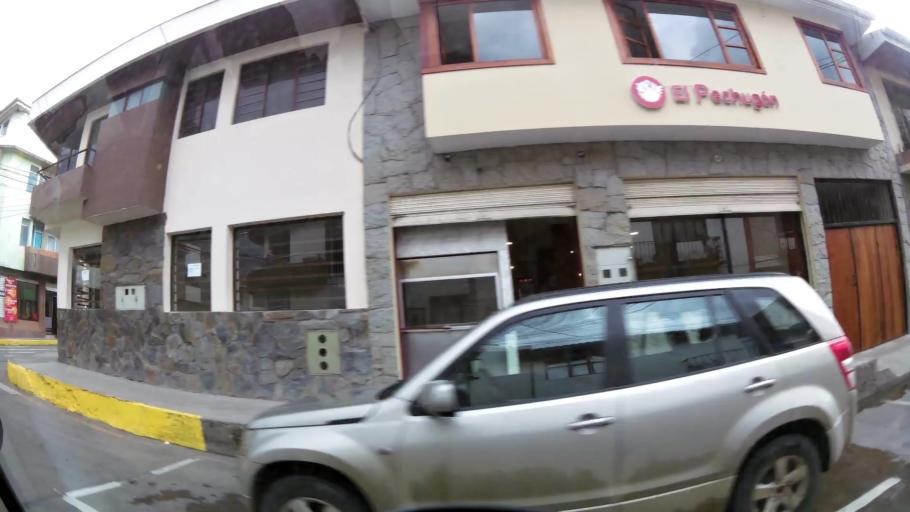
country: EC
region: Azuay
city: Cuenca
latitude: -2.8948
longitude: -79.0126
